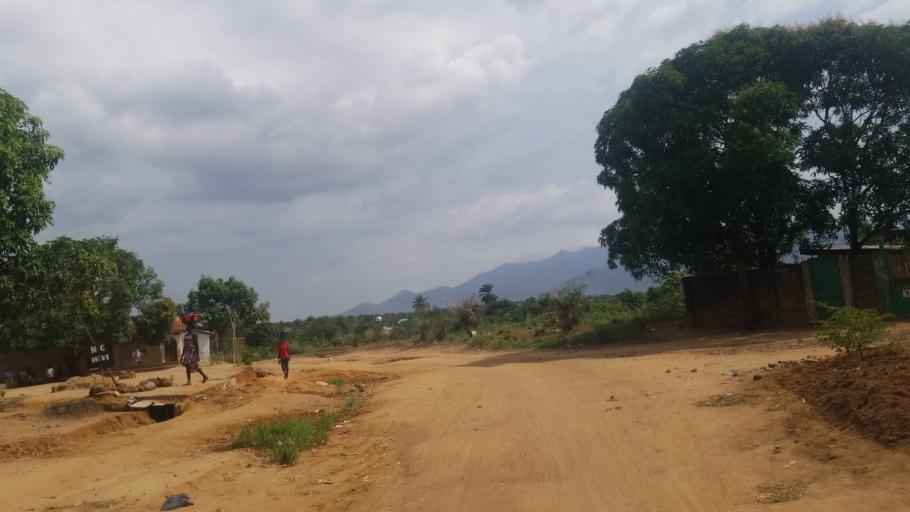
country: SL
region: Western Area
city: Waterloo
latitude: 8.3460
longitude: -13.0527
